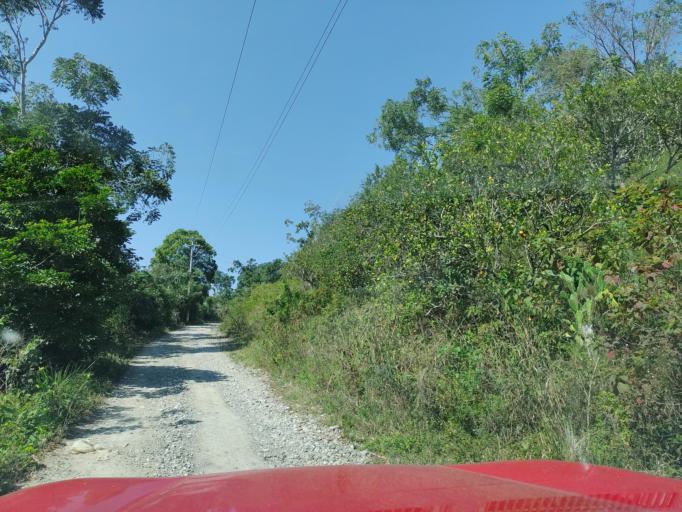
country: MX
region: Veracruz
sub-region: Papantla
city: Polutla
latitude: 20.5018
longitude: -97.2174
